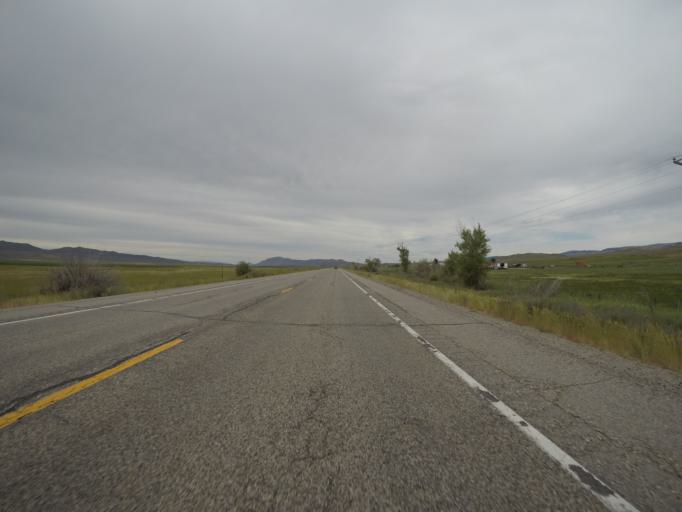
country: US
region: Utah
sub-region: Rich County
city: Randolph
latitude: 42.0066
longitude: -110.9372
